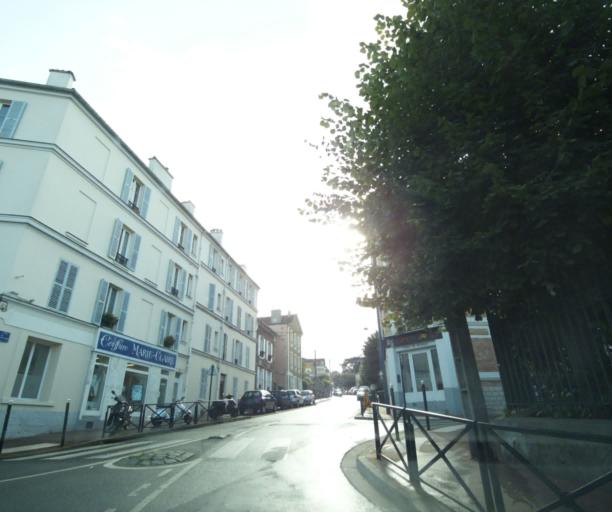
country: FR
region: Ile-de-France
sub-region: Departement des Hauts-de-Seine
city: Clamart
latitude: 48.8088
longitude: 2.2661
